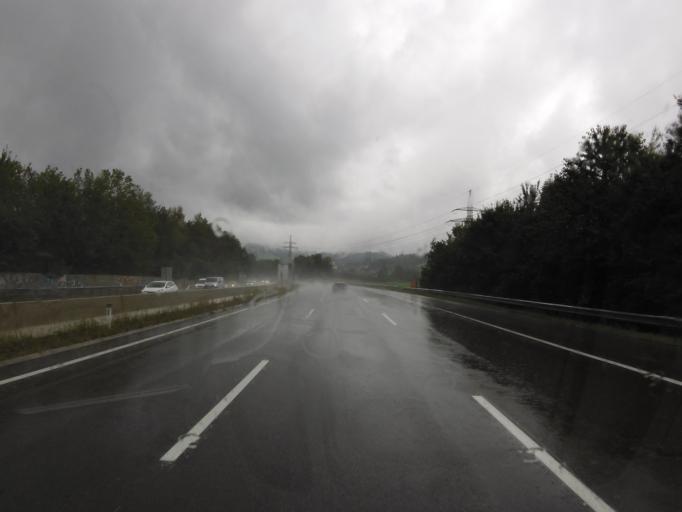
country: AT
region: Vorarlberg
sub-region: Politischer Bezirk Bregenz
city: Wolfurt
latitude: 47.4638
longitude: 9.7314
